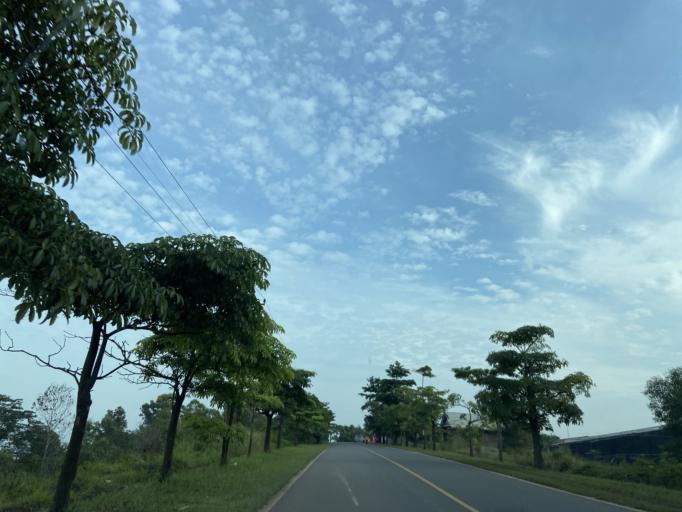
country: ID
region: Riau Islands
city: Tanjungpinang
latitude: 0.9250
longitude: 104.1159
